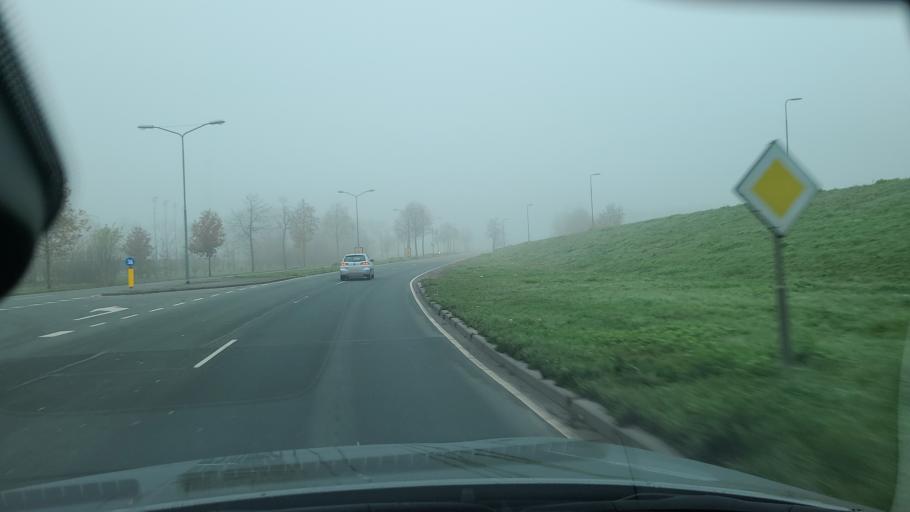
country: NL
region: North Brabant
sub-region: Gemeente 's-Hertogenbosch
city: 's-Hertogenbosch
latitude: 51.7202
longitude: 5.3457
